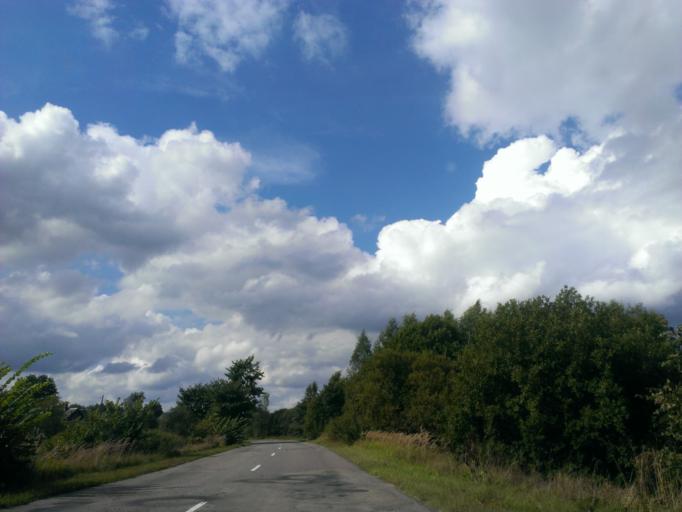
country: LV
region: Ropazu
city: Ropazi
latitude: 56.9606
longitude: 24.5419
